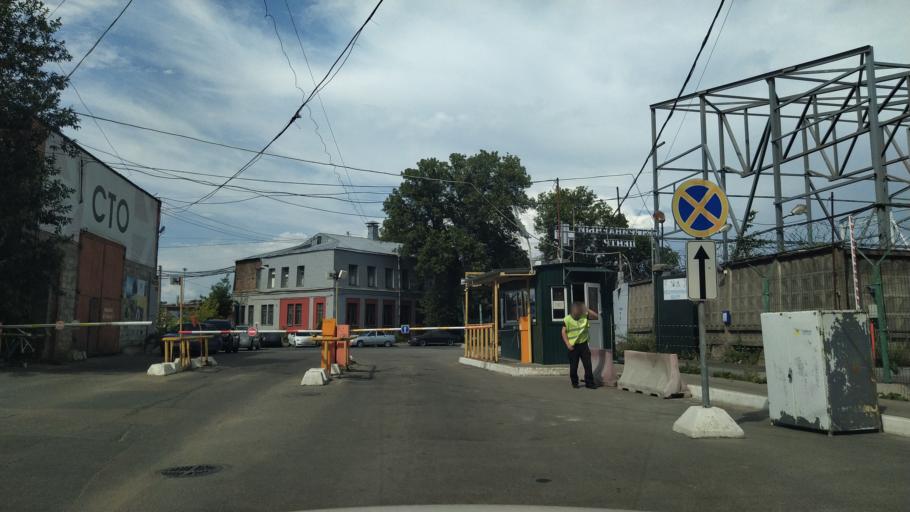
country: RU
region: Leningrad
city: Finlyandskiy
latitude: 59.9638
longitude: 30.3644
